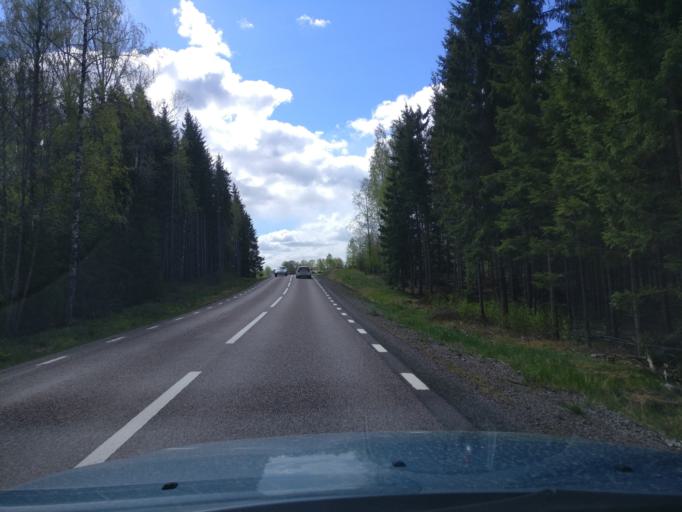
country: SE
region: Vaermland
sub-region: Karlstads Kommun
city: Molkom
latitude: 59.7246
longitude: 13.6785
